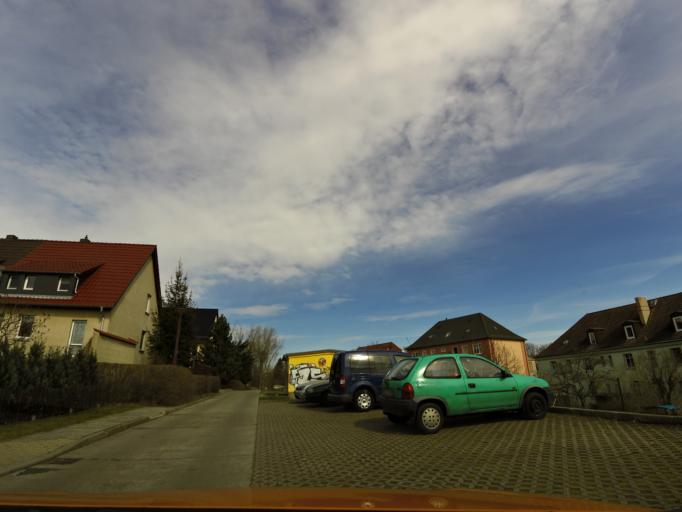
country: DE
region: Brandenburg
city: Belzig
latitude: 52.1446
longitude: 12.5893
